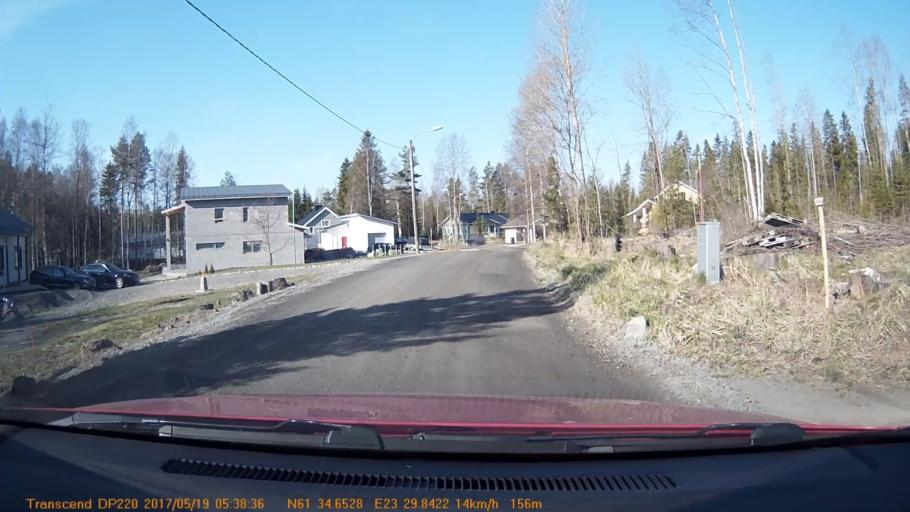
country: FI
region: Pirkanmaa
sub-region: Tampere
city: Yloejaervi
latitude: 61.5775
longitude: 23.4972
